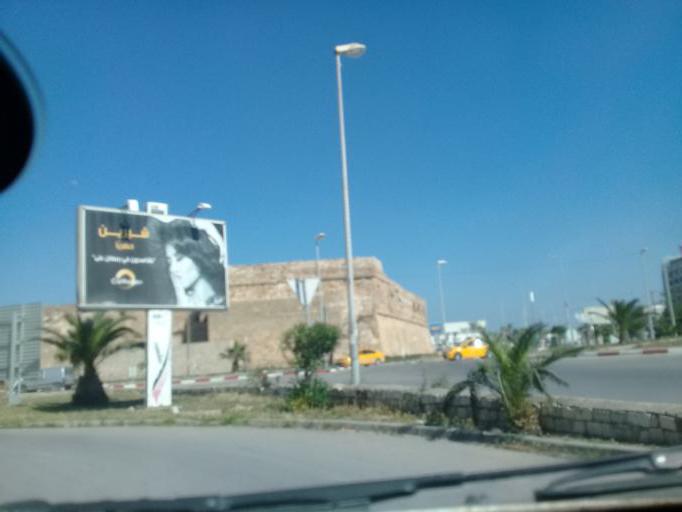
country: TN
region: Tunis
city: La Goulette
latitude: 36.8144
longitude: 10.3020
